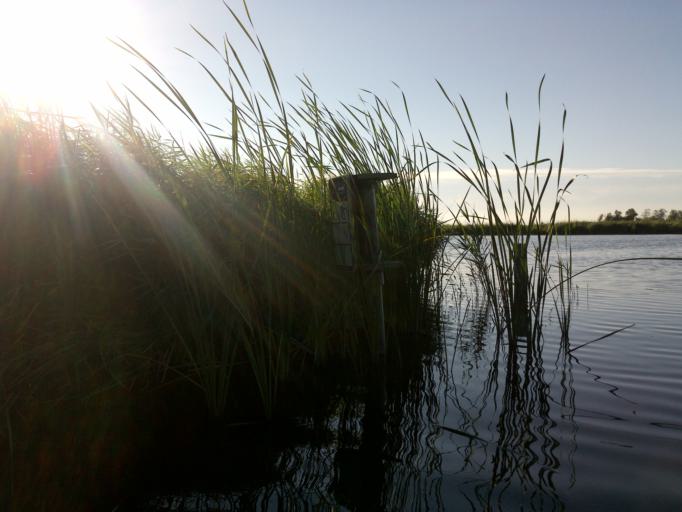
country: NL
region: North Holland
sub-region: Gemeente Beemster
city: Halfweg
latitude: 52.5630
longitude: 4.8310
